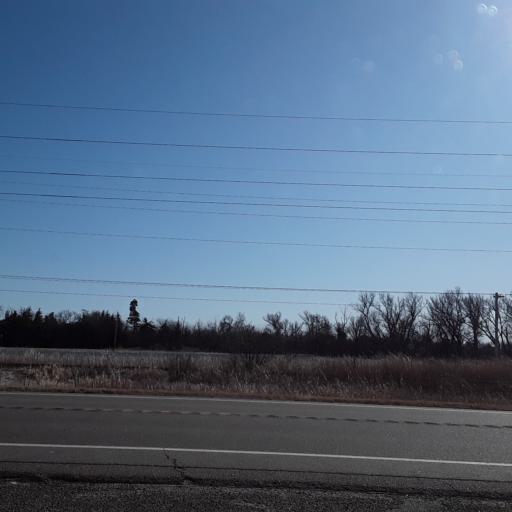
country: US
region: Kansas
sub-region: Pawnee County
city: Larned
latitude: 38.1642
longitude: -99.1156
